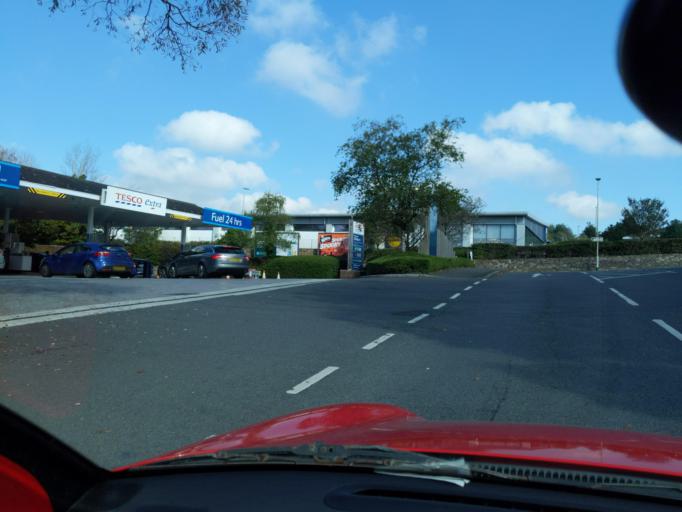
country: GB
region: England
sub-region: Devon
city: Yelverton
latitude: 50.4352
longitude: -4.1082
